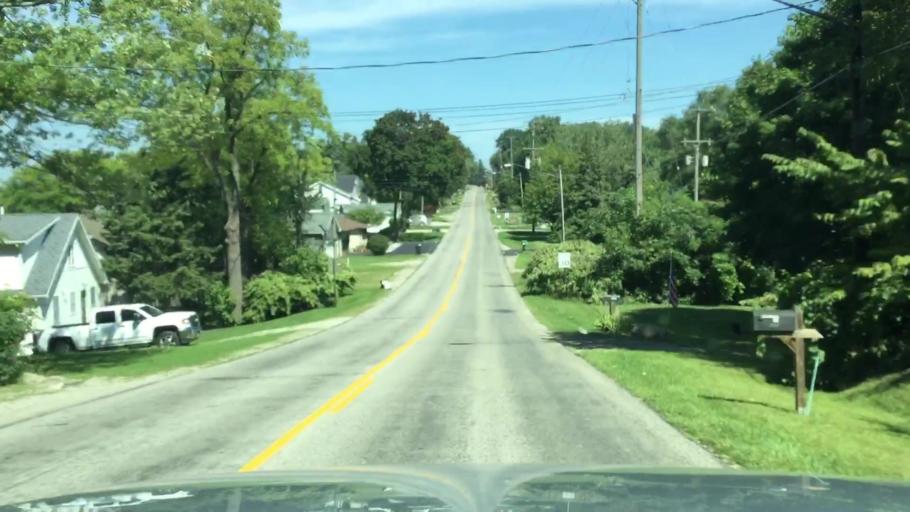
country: US
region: Michigan
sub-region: Lenawee County
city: Manitou Beach-Devils Lake
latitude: 41.9976
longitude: -84.2808
